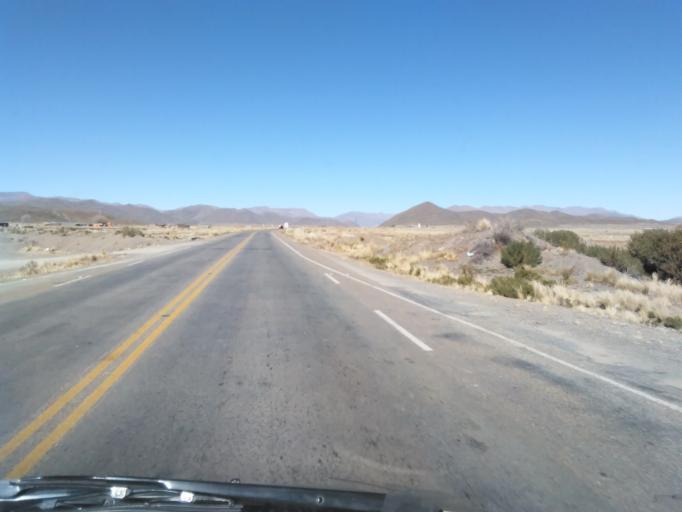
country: BO
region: Oruro
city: Machacamarca
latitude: -18.1552
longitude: -66.9758
